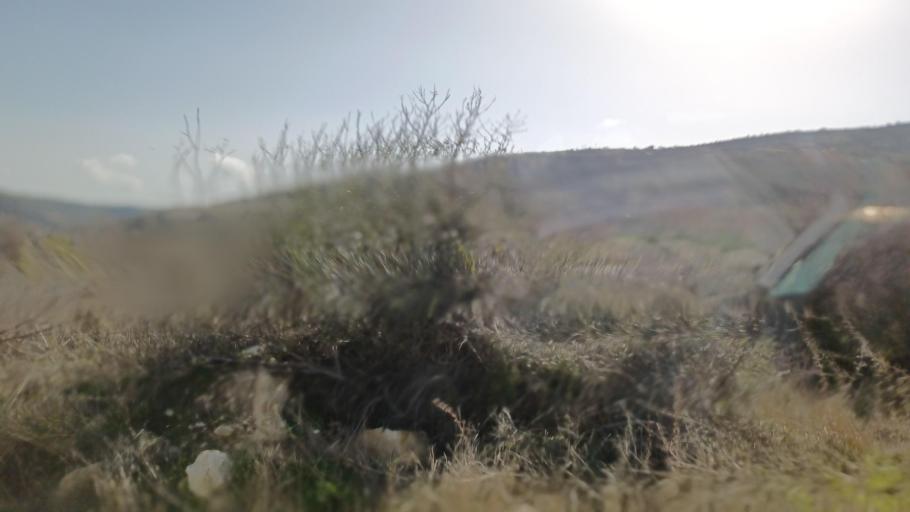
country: CY
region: Limassol
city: Pachna
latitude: 34.8452
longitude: 32.8128
